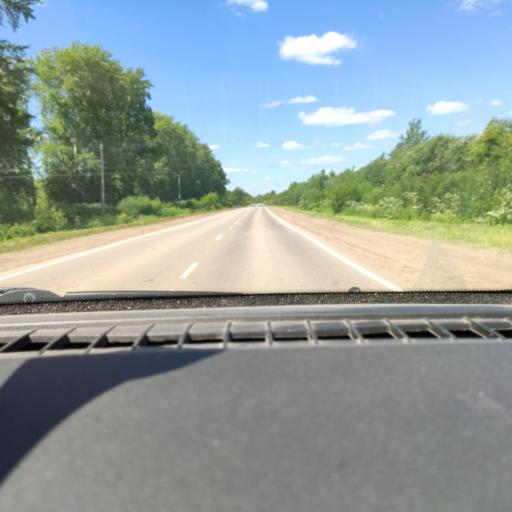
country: RU
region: Perm
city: Chaykovskaya
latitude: 58.1061
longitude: 55.5880
